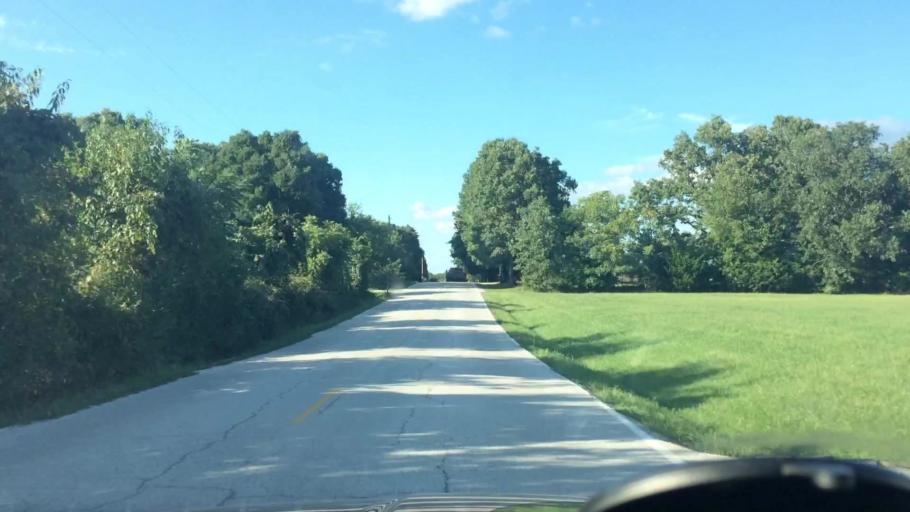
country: US
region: Missouri
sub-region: Greene County
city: Strafford
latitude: 37.2803
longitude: -93.0812
